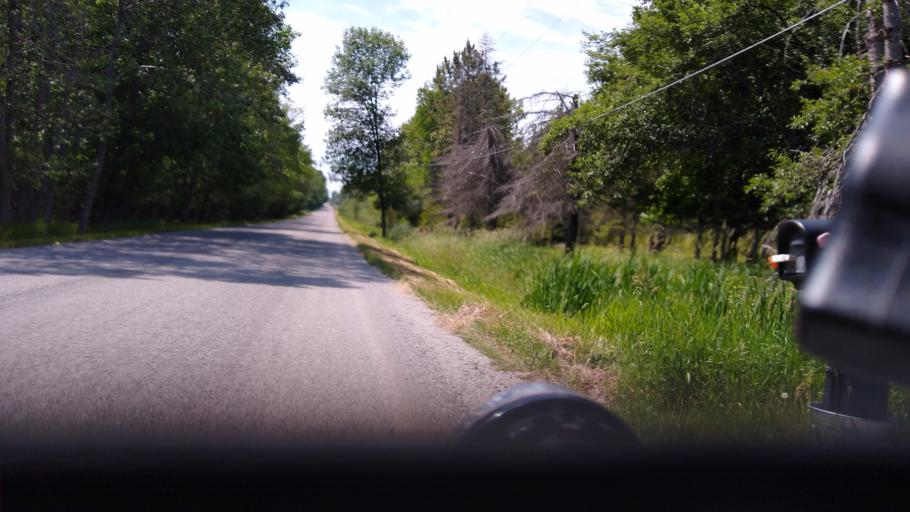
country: US
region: Michigan
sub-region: Delta County
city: Escanaba
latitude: 45.7102
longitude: -87.1336
